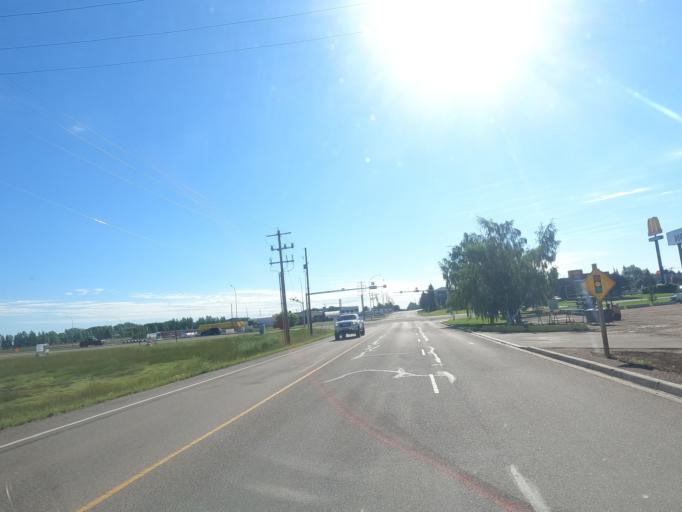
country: CA
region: Alberta
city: Brooks
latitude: 50.5867
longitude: -111.8986
